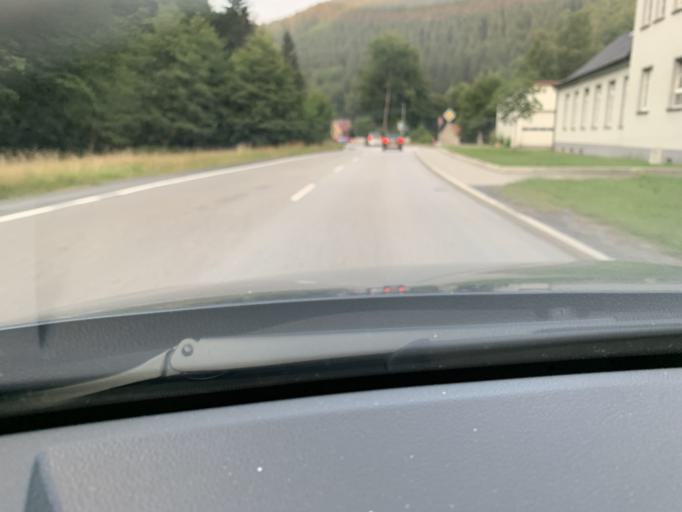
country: DE
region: Thuringia
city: Judenbach
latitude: 50.3840
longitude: 11.1990
